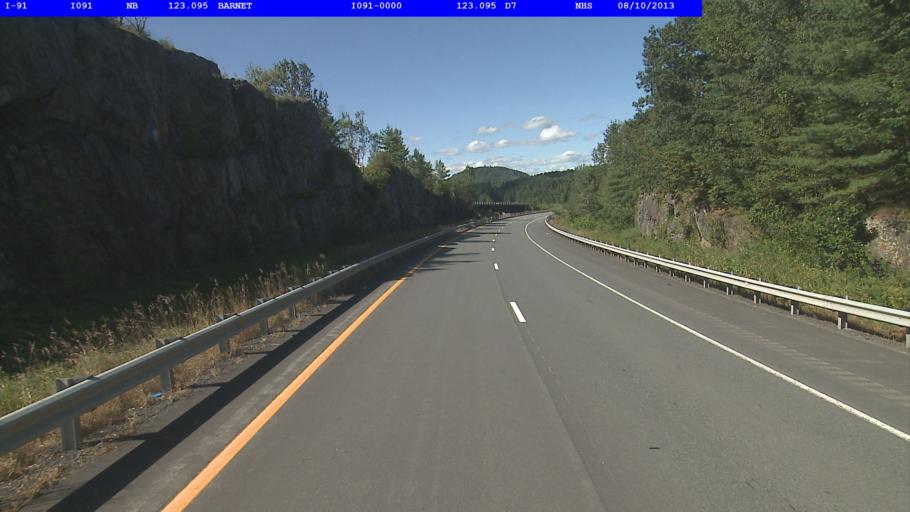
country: US
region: Vermont
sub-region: Caledonia County
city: Saint Johnsbury
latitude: 44.3261
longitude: -72.0396
